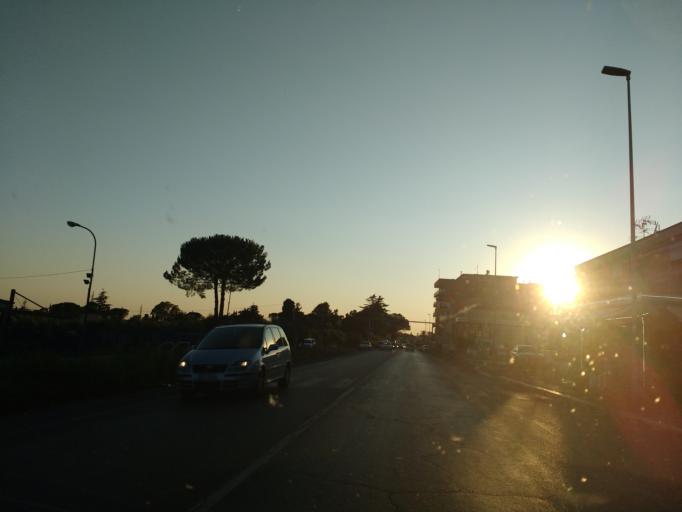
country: IT
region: Latium
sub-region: Citta metropolitana di Roma Capitale
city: Bagni di Tivoli
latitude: 41.9543
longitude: 12.7096
